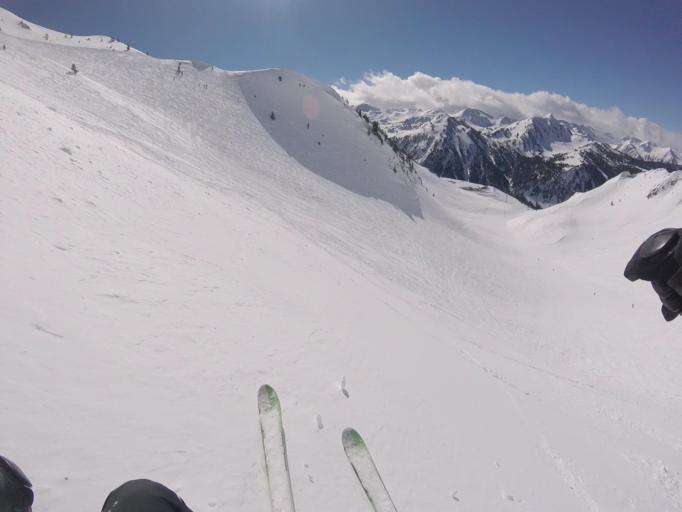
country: ES
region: Catalonia
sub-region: Provincia de Lleida
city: Espot
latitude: 42.6709
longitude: 0.9872
